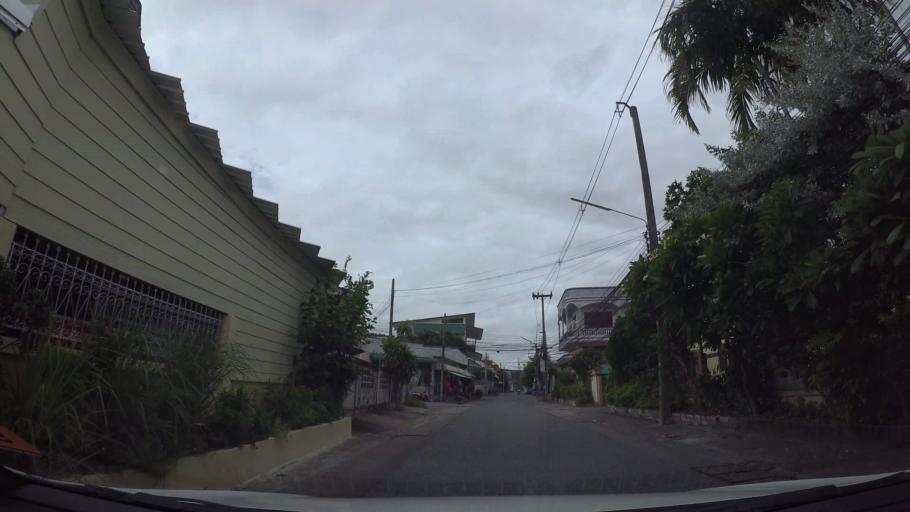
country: TH
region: Rayong
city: Rayong
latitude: 12.6726
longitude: 101.2739
